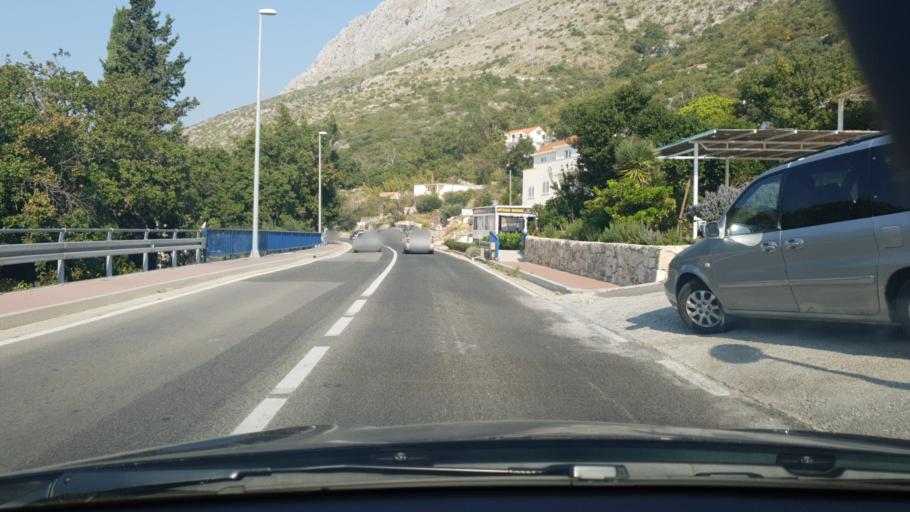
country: HR
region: Dubrovacko-Neretvanska
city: Cavtat
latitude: 42.6114
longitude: 18.2276
